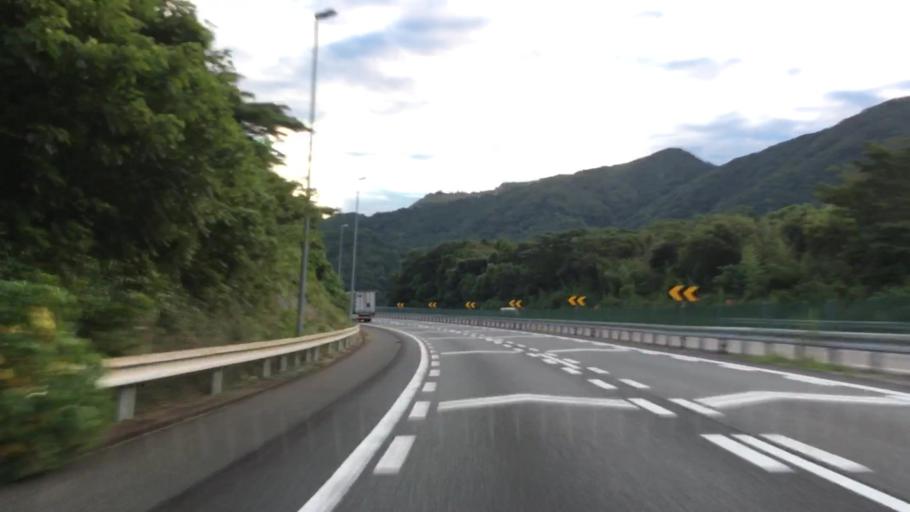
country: JP
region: Yamaguchi
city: Shimonoseki
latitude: 34.0360
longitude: 130.9649
